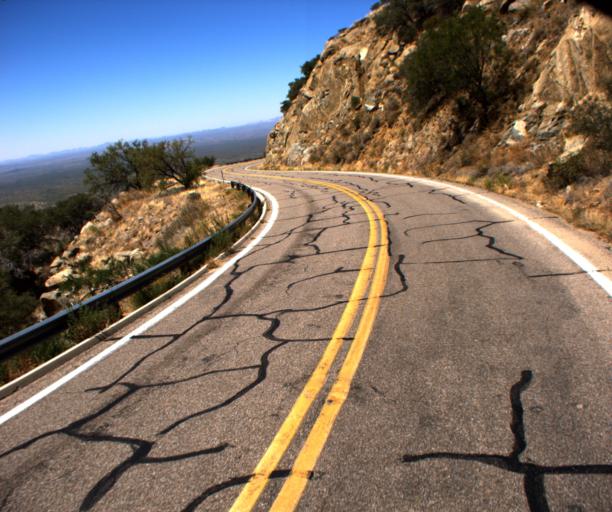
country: US
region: Arizona
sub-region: Pima County
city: Sells
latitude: 31.9732
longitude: -111.6094
